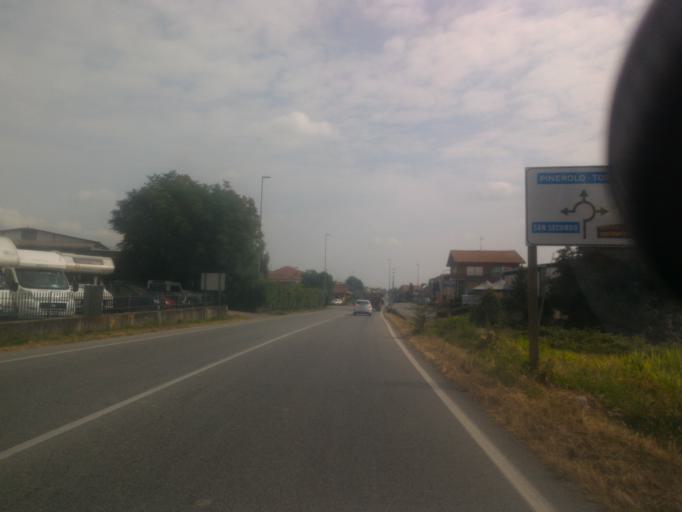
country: IT
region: Piedmont
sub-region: Provincia di Torino
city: Bricherasio
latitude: 44.8388
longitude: 7.3059
